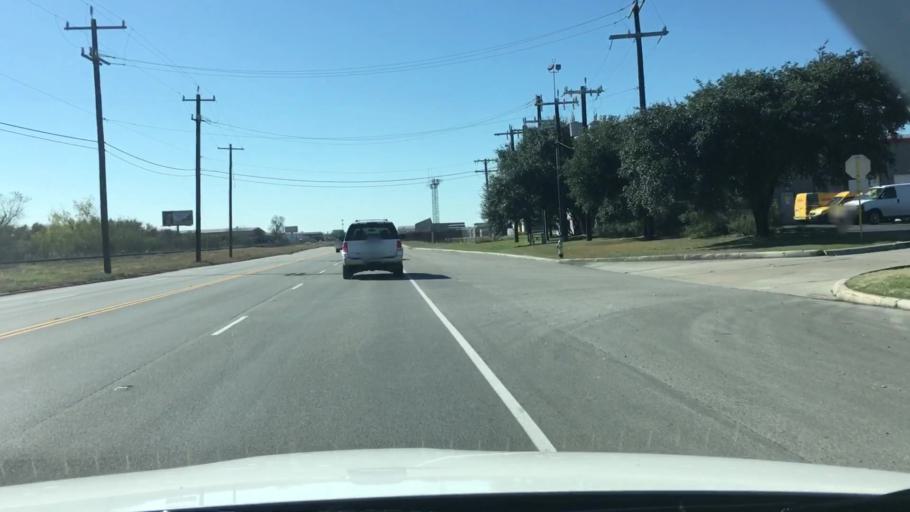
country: US
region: Texas
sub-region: Bexar County
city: Alamo Heights
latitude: 29.5313
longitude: -98.4567
